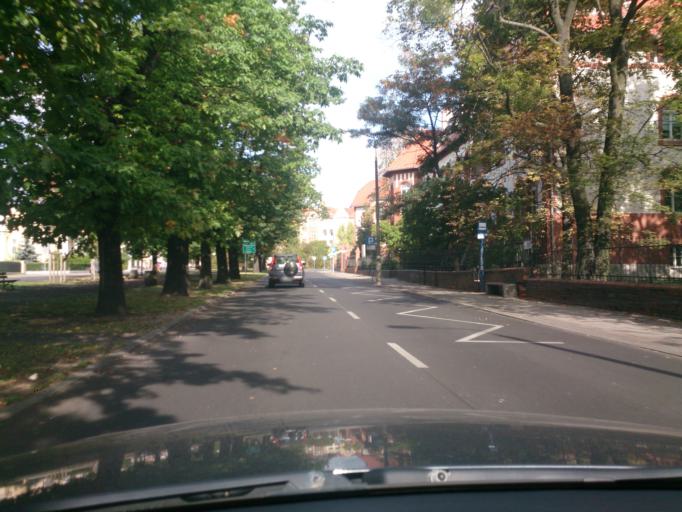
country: PL
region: Kujawsko-Pomorskie
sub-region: Bydgoszcz
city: Bydgoszcz
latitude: 53.1285
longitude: 18.0156
